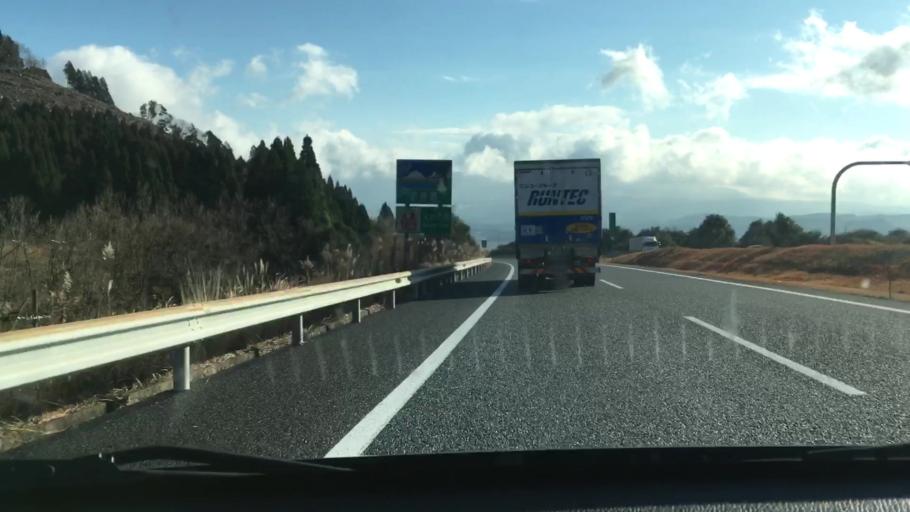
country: JP
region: Kumamoto
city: Hitoyoshi
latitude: 32.0755
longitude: 130.7930
